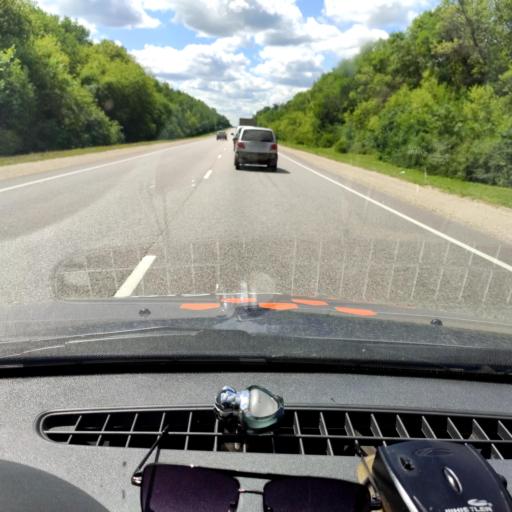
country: RU
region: Lipetsk
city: Borinskoye
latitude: 52.3861
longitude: 39.2240
